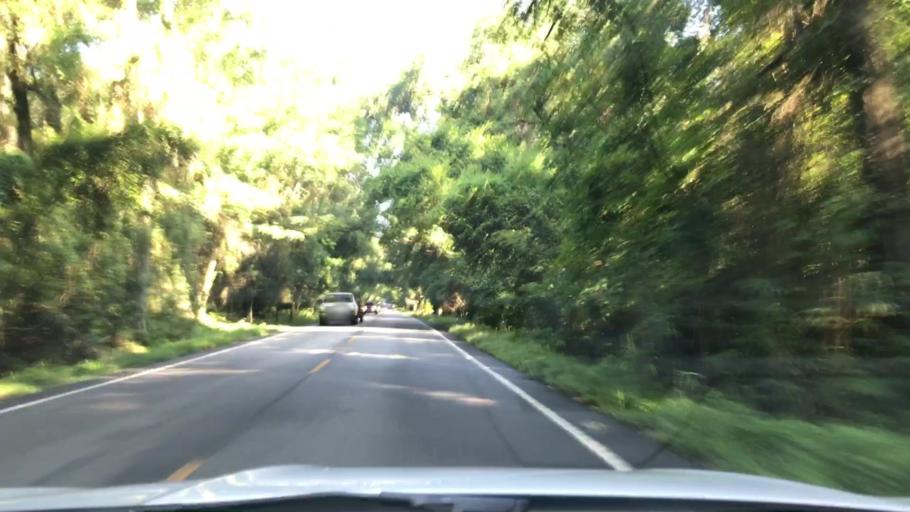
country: US
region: South Carolina
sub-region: Charleston County
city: Shell Point
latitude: 32.8669
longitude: -80.0854
